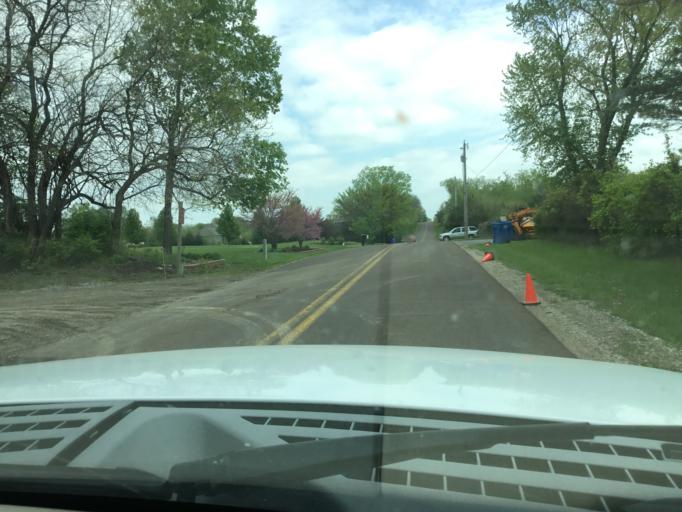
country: US
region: Kansas
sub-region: Shawnee County
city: Auburn
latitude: 38.9708
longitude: -95.7856
